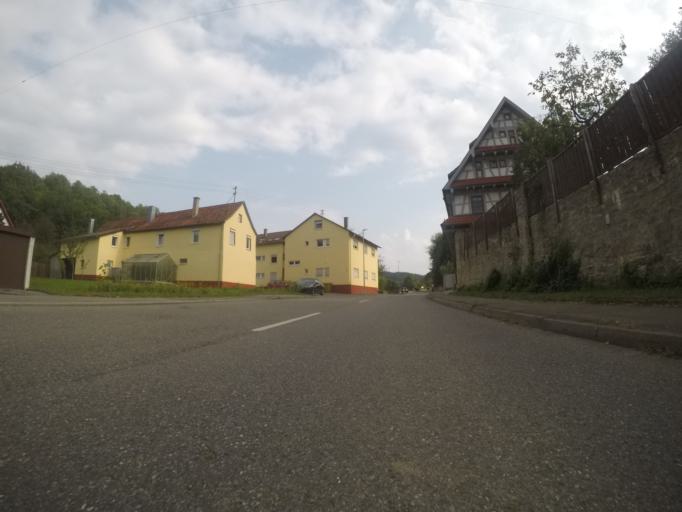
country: DE
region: Baden-Wuerttemberg
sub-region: Regierungsbezirk Stuttgart
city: Eberdingen
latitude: 48.8743
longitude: 8.9643
